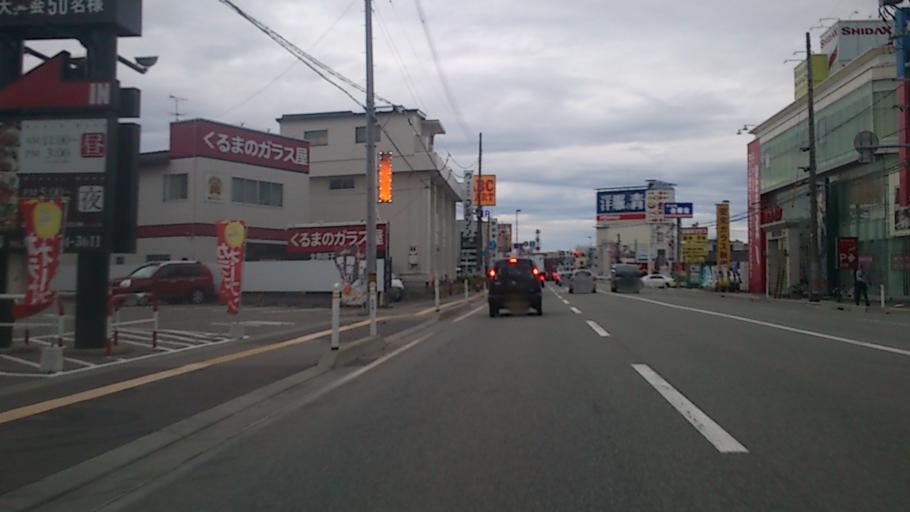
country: JP
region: Akita
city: Akita Shi
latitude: 39.7299
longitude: 140.1038
